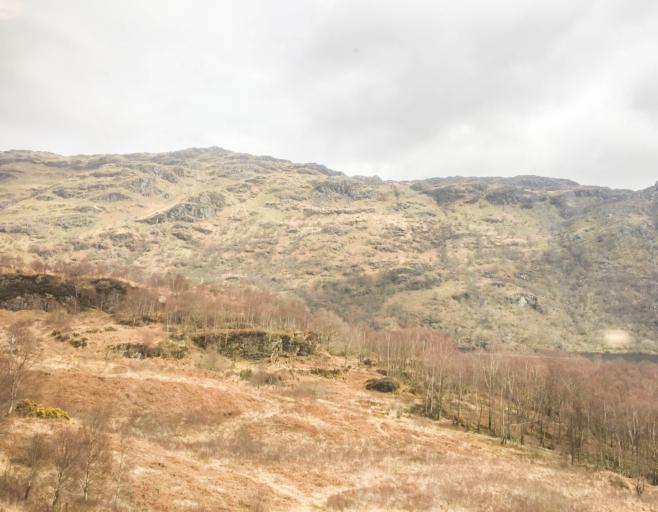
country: GB
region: Scotland
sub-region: Argyll and Bute
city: Garelochhead
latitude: 56.2798
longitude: -4.7057
